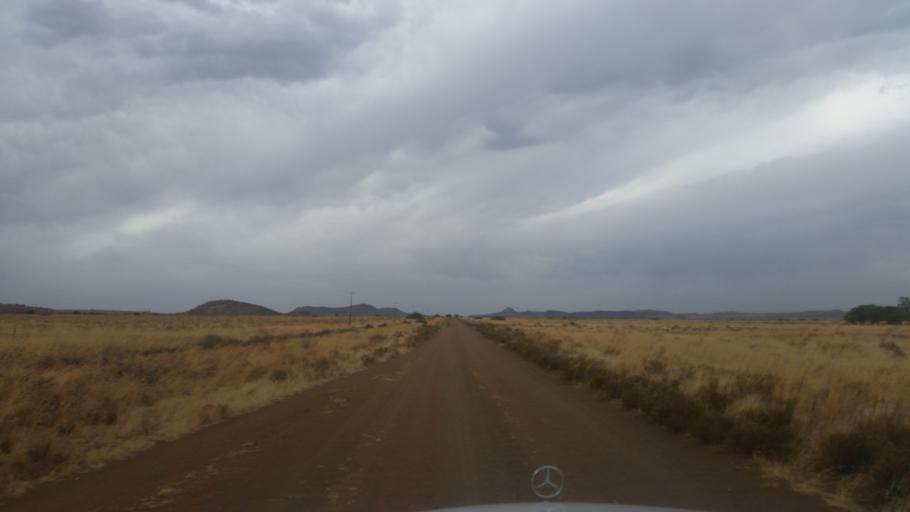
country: ZA
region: Orange Free State
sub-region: Xhariep District Municipality
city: Trompsburg
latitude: -30.5059
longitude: 25.9420
